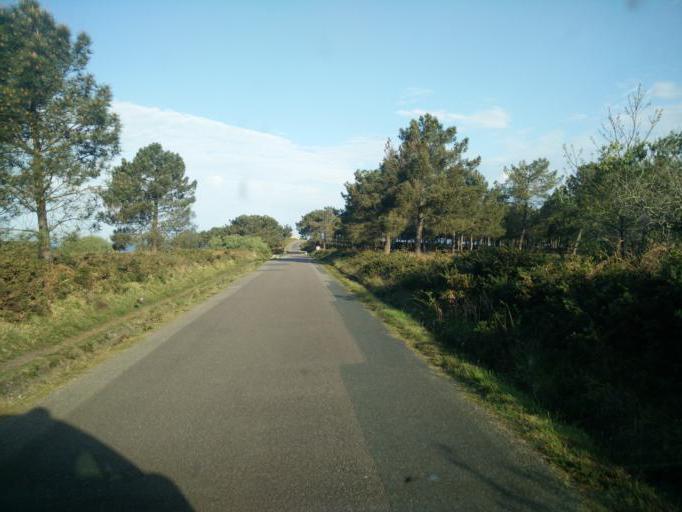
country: FR
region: Brittany
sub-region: Departement des Cotes-d'Armor
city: Erquy
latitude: 48.6387
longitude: -2.4779
